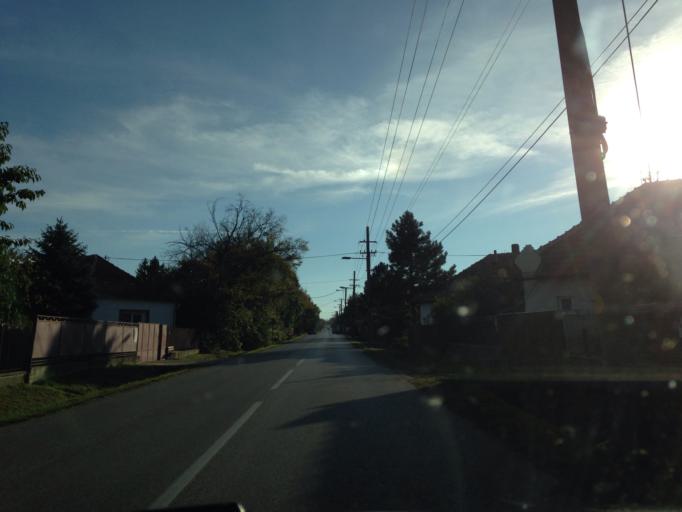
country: SK
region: Nitriansky
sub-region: Okres Komarno
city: Hurbanovo
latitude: 47.9005
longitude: 18.3067
